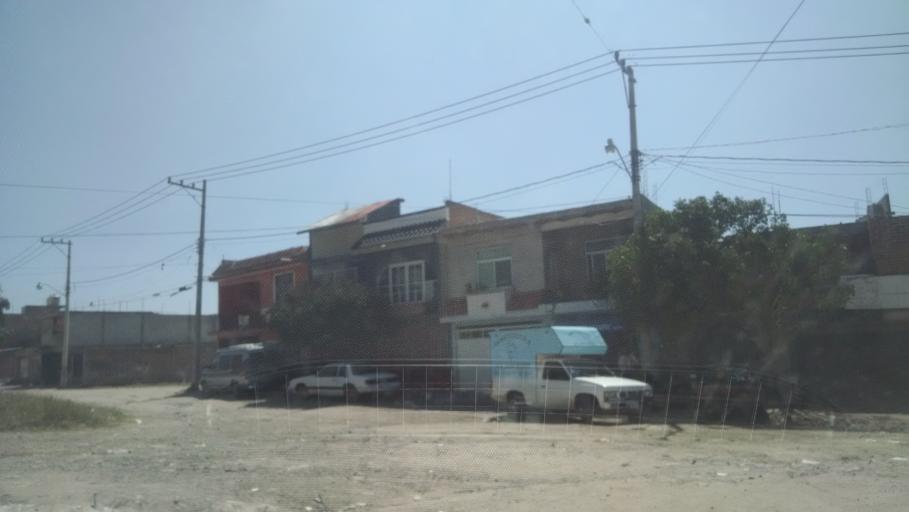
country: MX
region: Guanajuato
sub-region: Leon
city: La Ermita
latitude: 21.1494
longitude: -101.7353
